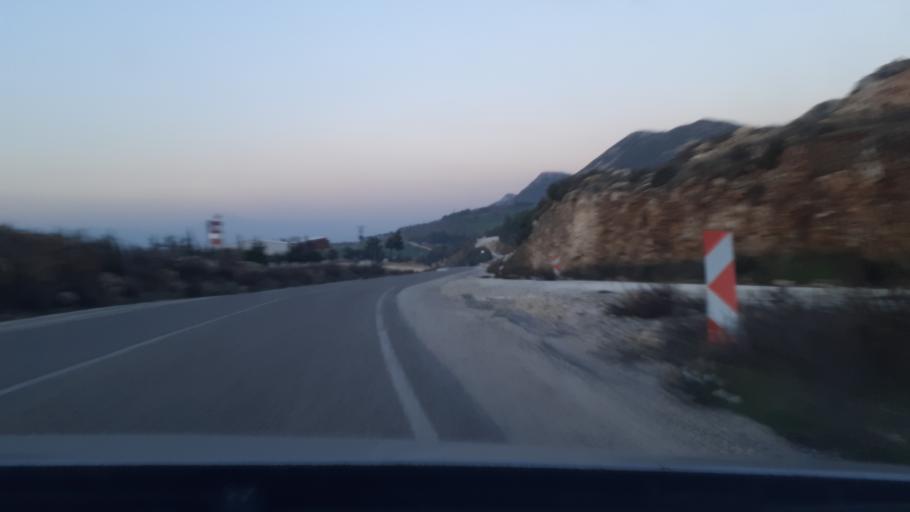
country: TR
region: Hatay
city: Dursunlu
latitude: 36.1732
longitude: 36.1864
